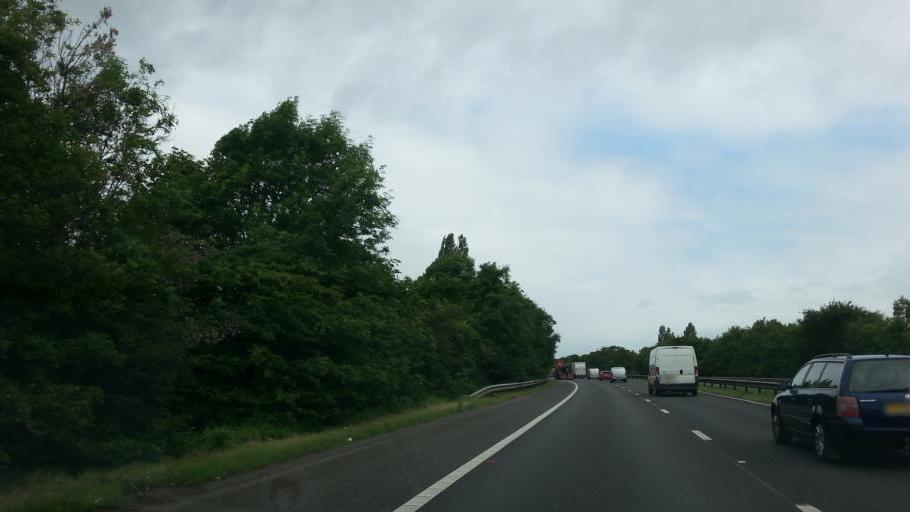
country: GB
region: England
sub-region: Doncaster
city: Tickhill
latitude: 53.4308
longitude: -1.0947
